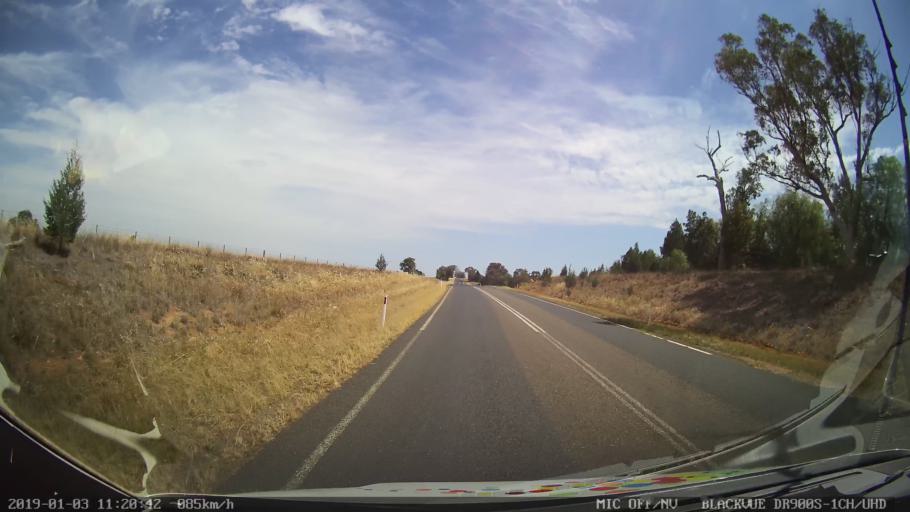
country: AU
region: New South Wales
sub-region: Young
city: Young
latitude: -34.0978
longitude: 148.2540
